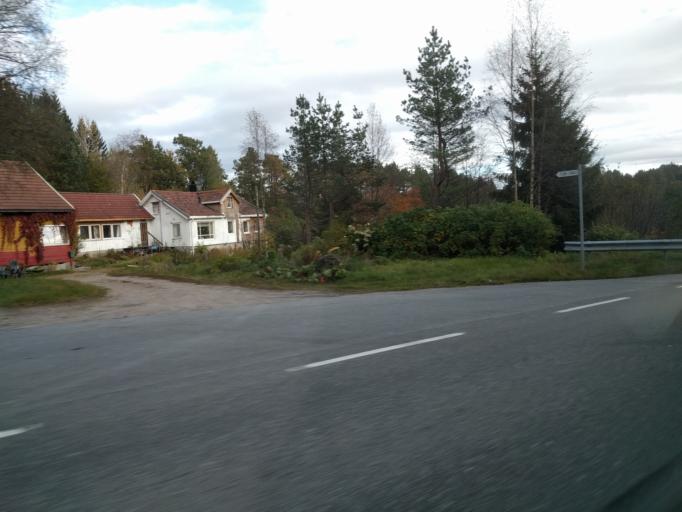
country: NO
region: Vest-Agder
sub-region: Kristiansand
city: Strai
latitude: 58.2537
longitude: 7.8525
